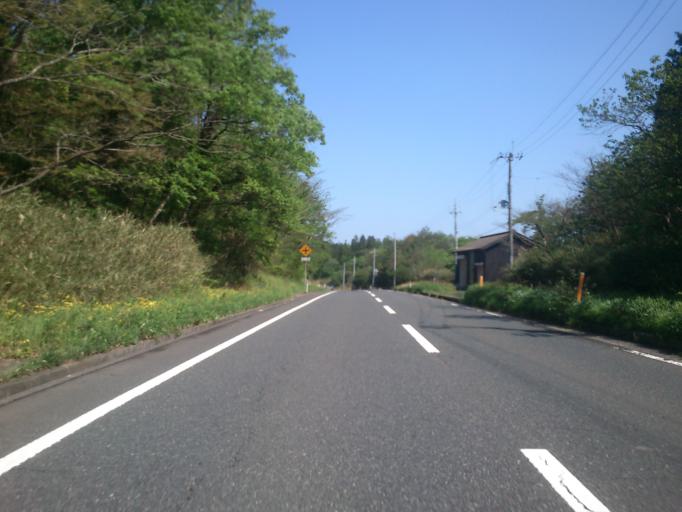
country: JP
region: Kyoto
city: Miyazu
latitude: 35.6641
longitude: 135.1028
